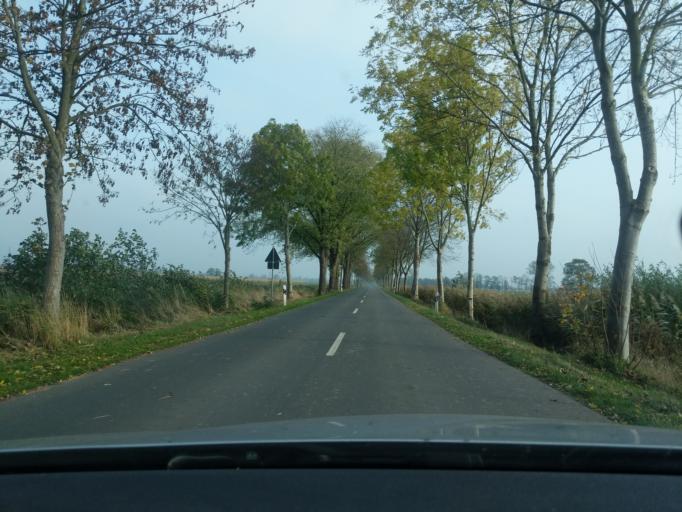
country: DE
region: Lower Saxony
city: Ihlienworth
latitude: 53.7234
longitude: 8.9342
